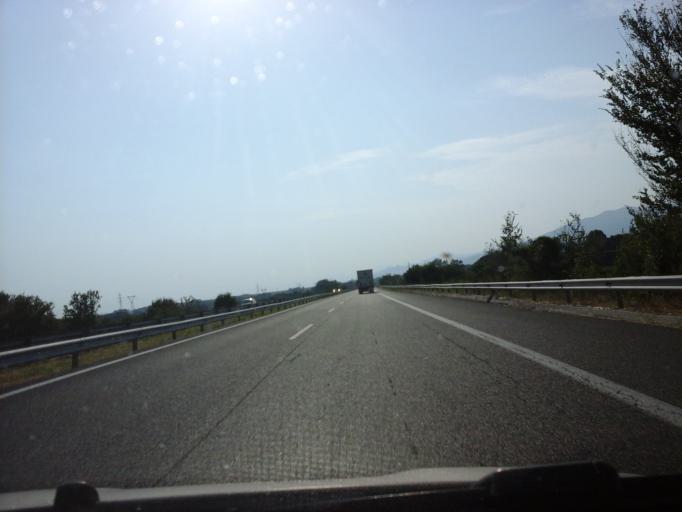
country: GR
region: East Macedonia and Thrace
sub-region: Nomos Rodopis
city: Komotini
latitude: 41.0964
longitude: 25.3893
